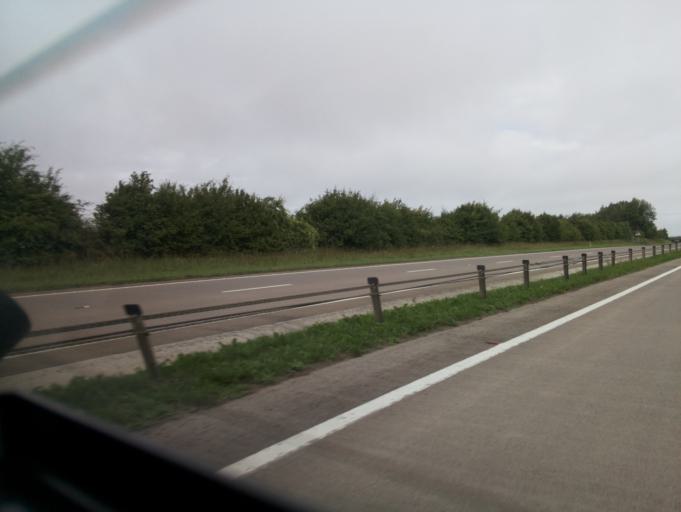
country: GB
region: England
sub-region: Gloucestershire
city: Cirencester
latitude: 51.7361
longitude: -1.9566
